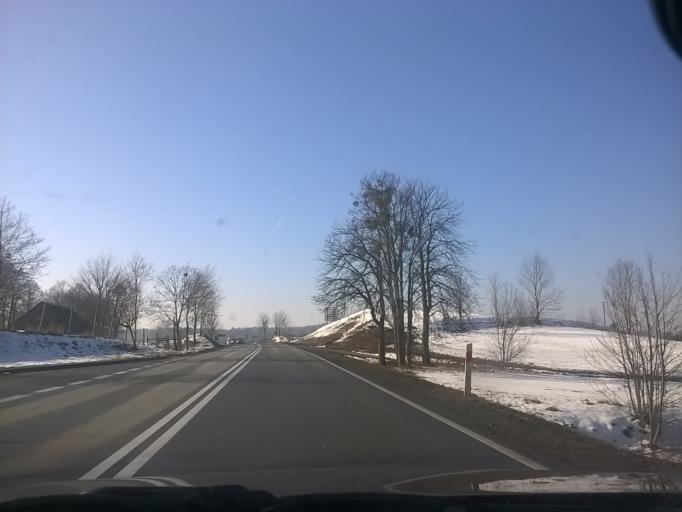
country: PL
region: Warmian-Masurian Voivodeship
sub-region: Powiat mragowski
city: Mragowo
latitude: 53.8391
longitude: 21.2072
